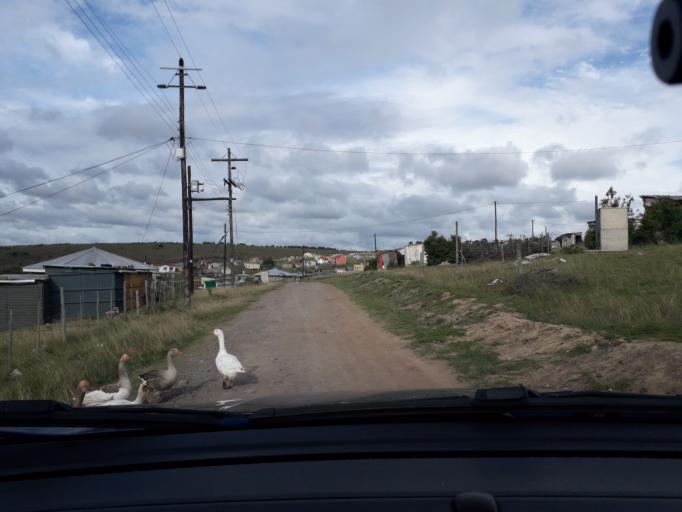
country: ZA
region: Eastern Cape
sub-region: Buffalo City Metropolitan Municipality
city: East London
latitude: -32.8501
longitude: 27.9863
